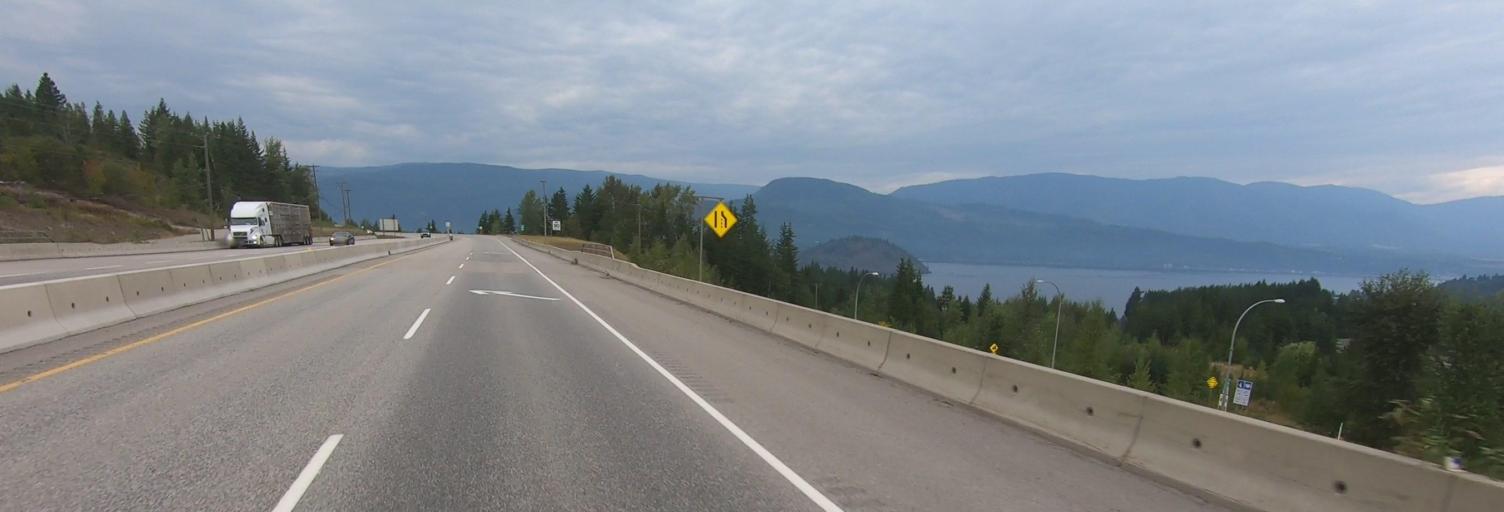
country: CA
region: British Columbia
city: Salmon Arm
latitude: 50.8763
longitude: -119.3901
